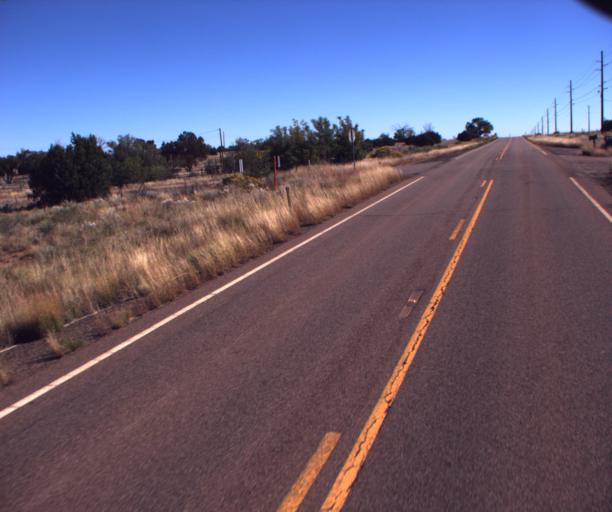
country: US
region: Arizona
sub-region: Navajo County
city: Taylor
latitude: 34.4844
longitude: -110.2549
